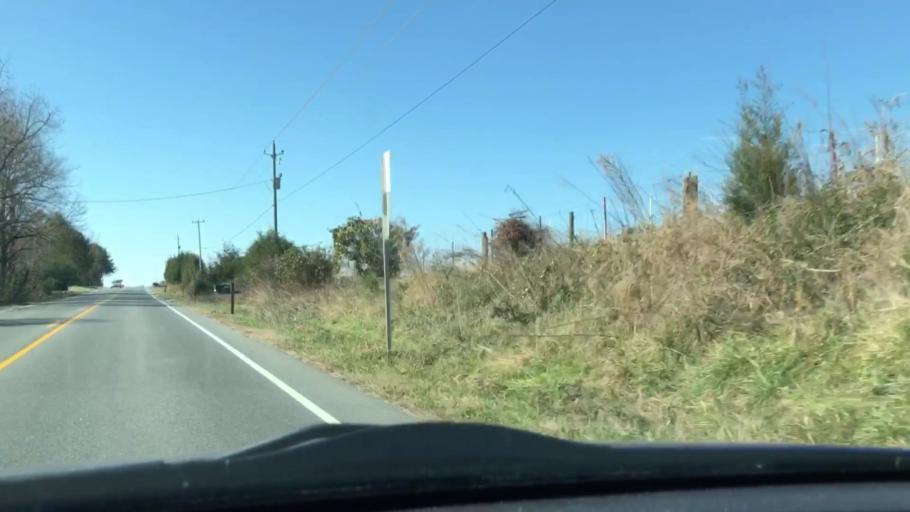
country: US
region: North Carolina
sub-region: Randolph County
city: Asheboro
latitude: 35.6828
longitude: -79.8570
